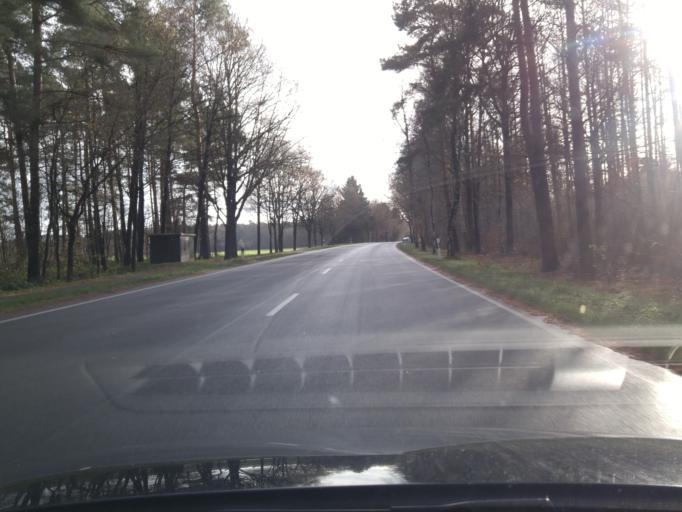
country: DE
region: Lower Saxony
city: Wietzendorf
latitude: 52.9177
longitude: 9.9133
